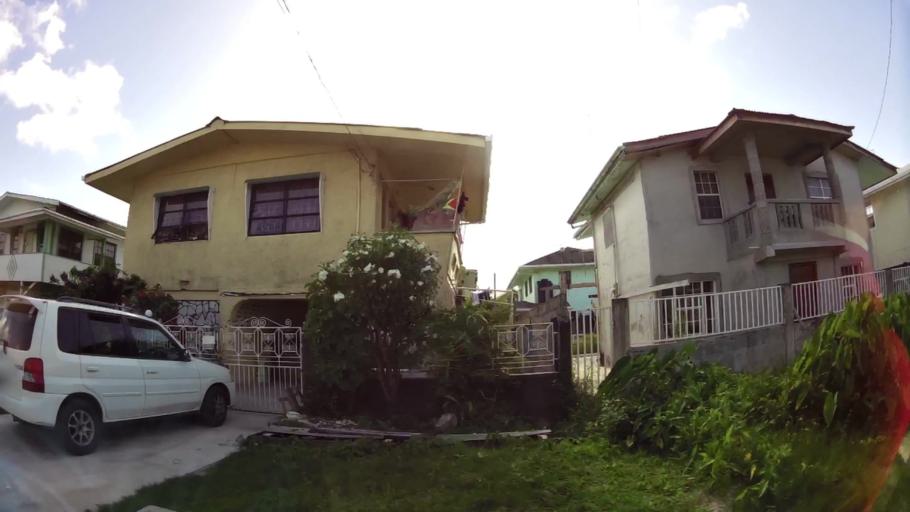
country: GY
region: Demerara-Mahaica
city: Georgetown
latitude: 6.8162
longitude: -58.1300
